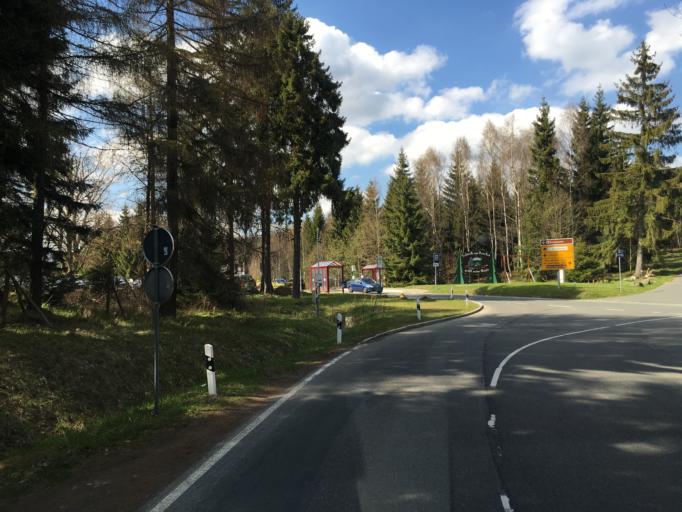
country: DE
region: Lower Saxony
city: Braunlage
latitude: 51.7566
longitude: 10.6843
